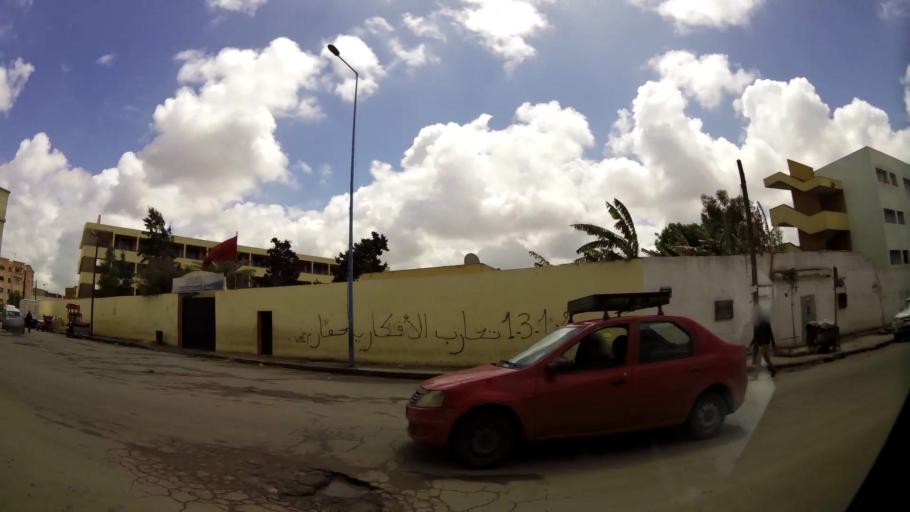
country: MA
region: Grand Casablanca
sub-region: Casablanca
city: Casablanca
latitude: 33.5738
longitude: -7.5924
